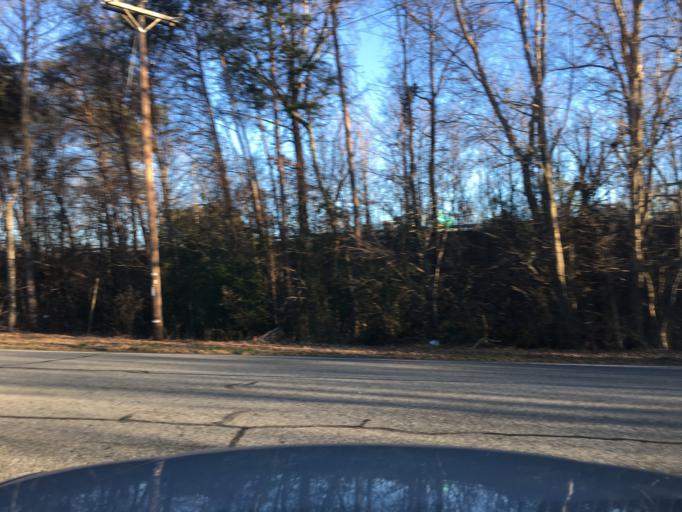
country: US
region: South Carolina
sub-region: Greenville County
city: Greenville
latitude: 34.8579
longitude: -82.3600
